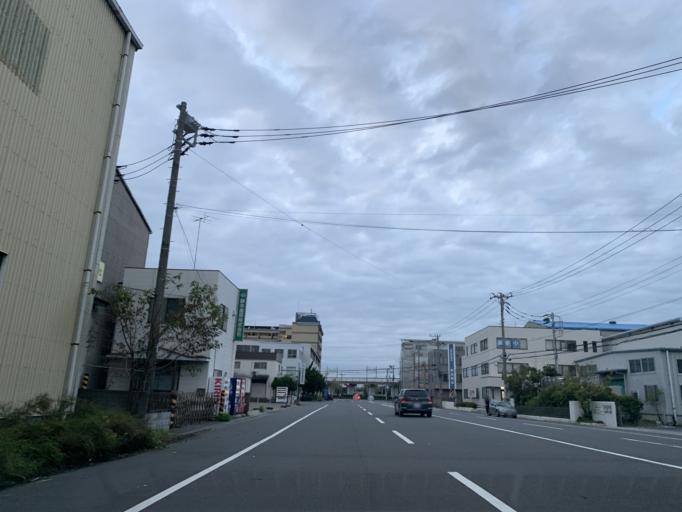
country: JP
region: Tokyo
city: Urayasu
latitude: 35.6319
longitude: 139.8940
